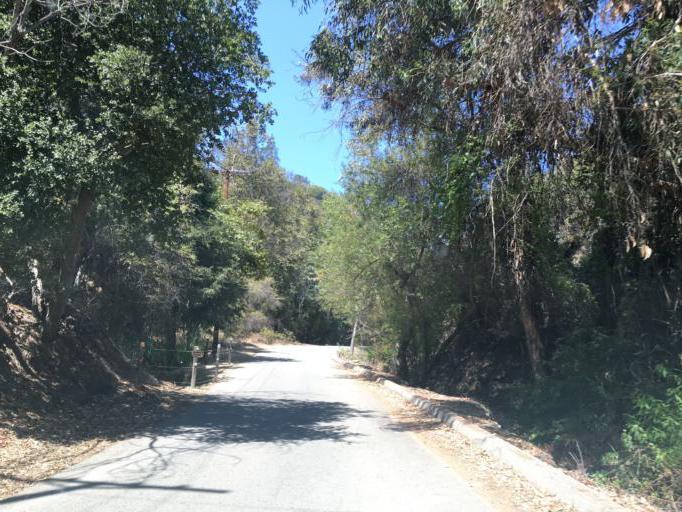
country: US
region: California
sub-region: Los Angeles County
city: Beverly Hills
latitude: 34.1122
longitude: -118.4152
